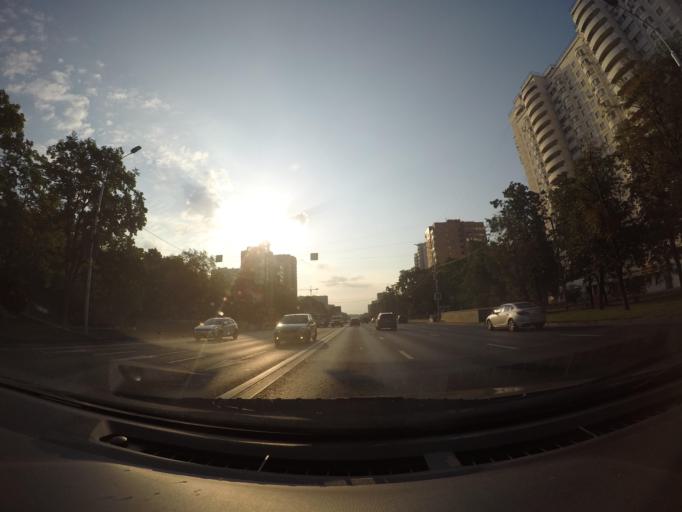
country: RU
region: Moscow
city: Novokuz'minki
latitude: 55.7042
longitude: 37.7742
